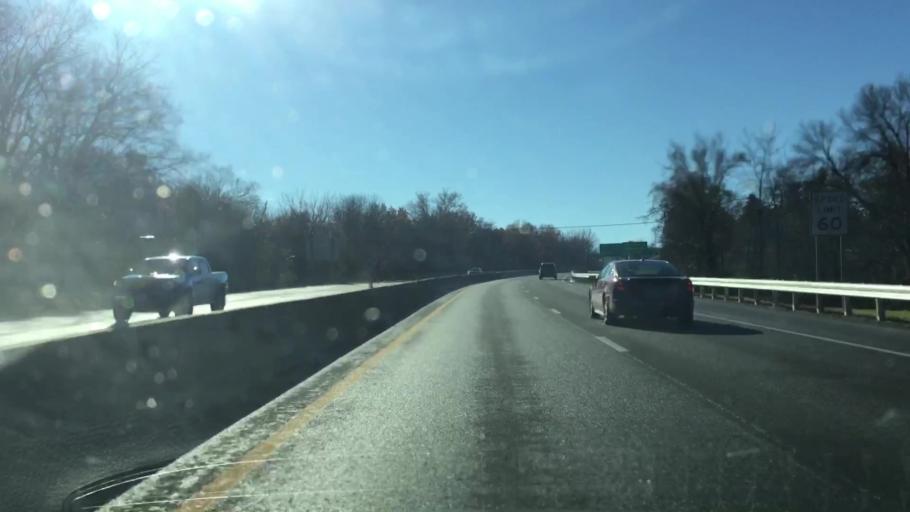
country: US
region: Missouri
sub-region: Cole County
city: Jefferson City
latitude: 38.5724
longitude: -92.1842
